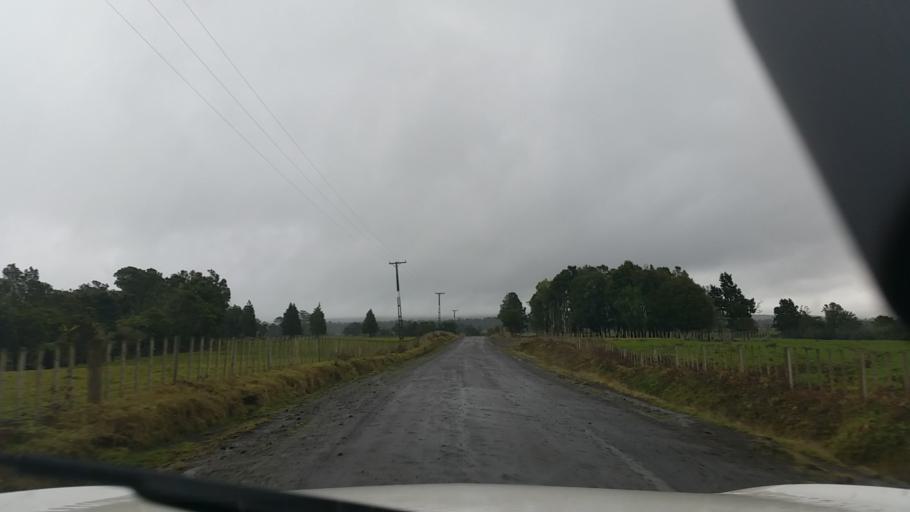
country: NZ
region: Taranaki
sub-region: South Taranaki District
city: Eltham
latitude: -39.2725
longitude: 174.1964
